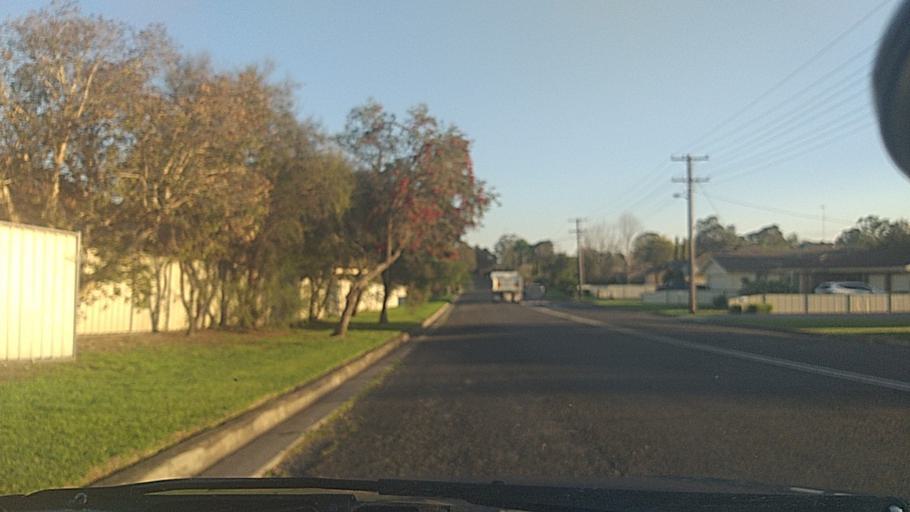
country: AU
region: New South Wales
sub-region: Wollondilly
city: Douglas Park
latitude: -34.1839
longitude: 150.7109
